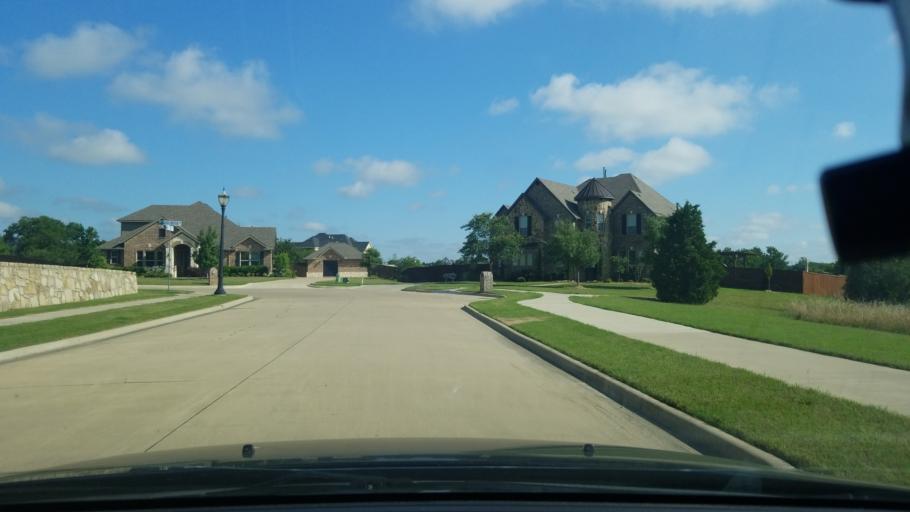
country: US
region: Texas
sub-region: Dallas County
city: Sunnyvale
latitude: 32.8082
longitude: -96.5650
